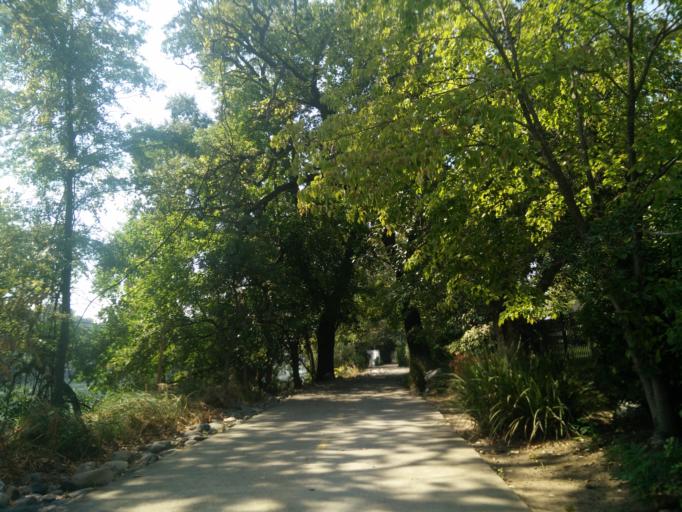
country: US
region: California
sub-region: Shasta County
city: Redding
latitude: 40.5940
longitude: -122.4037
